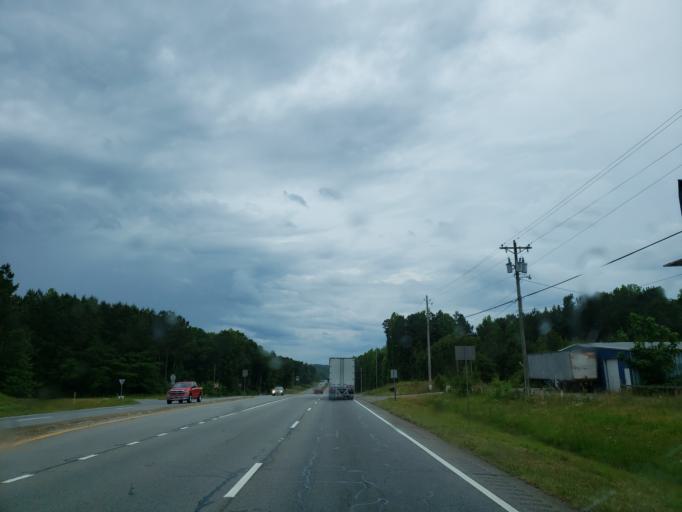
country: US
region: Georgia
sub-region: Haralson County
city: Buchanan
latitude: 33.7693
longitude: -85.1696
